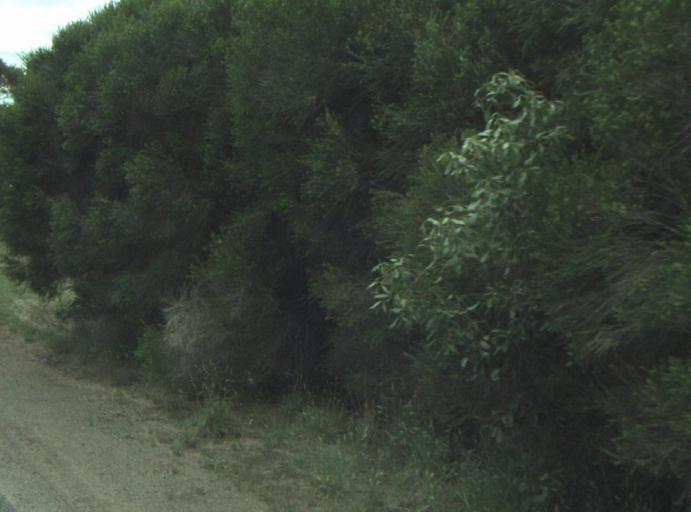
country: AU
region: Victoria
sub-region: Greater Geelong
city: Leopold
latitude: -38.2132
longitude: 144.4501
